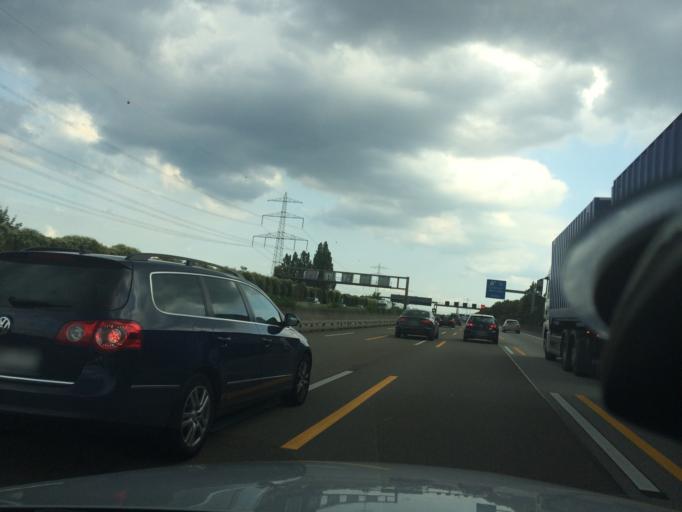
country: DE
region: Hesse
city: Niederrad
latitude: 50.1032
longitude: 8.6072
